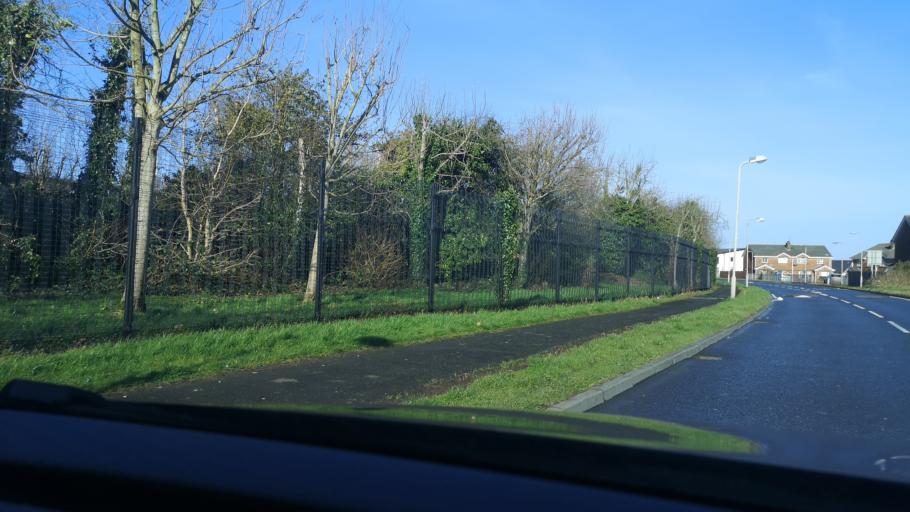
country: GB
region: Northern Ireland
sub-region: Newry and Mourne District
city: Newry
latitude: 54.1780
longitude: -6.3535
